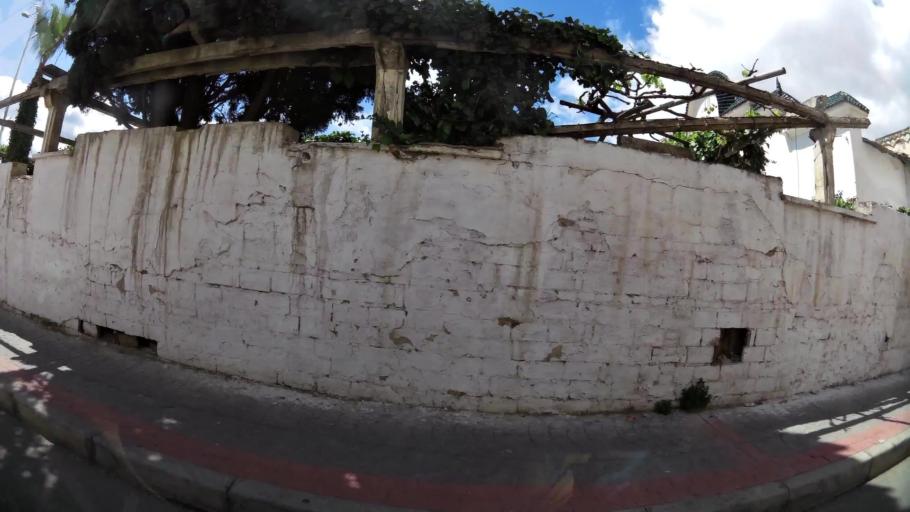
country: MA
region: Tanger-Tetouan
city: Tetouan
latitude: 35.5754
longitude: -5.3438
